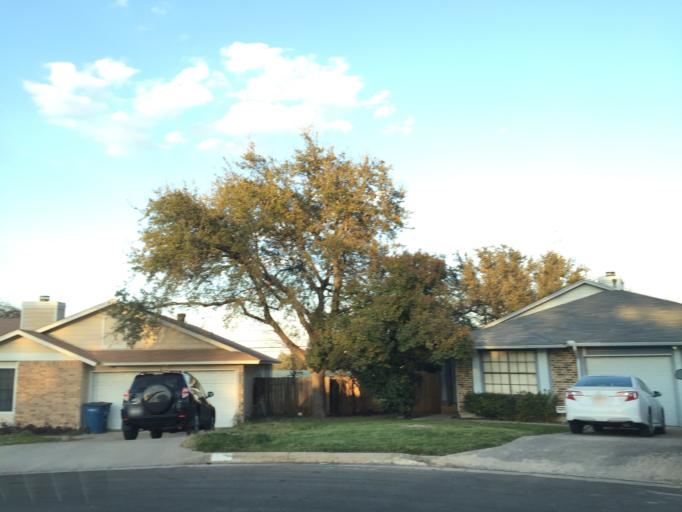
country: US
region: Texas
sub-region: Williamson County
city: Jollyville
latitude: 30.4371
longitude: -97.7370
